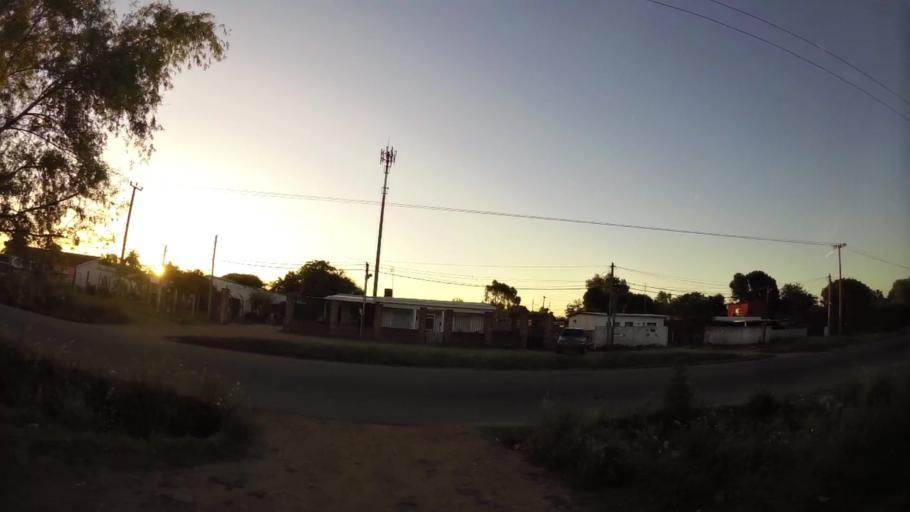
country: UY
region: Canelones
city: La Paz
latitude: -34.8202
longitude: -56.1688
